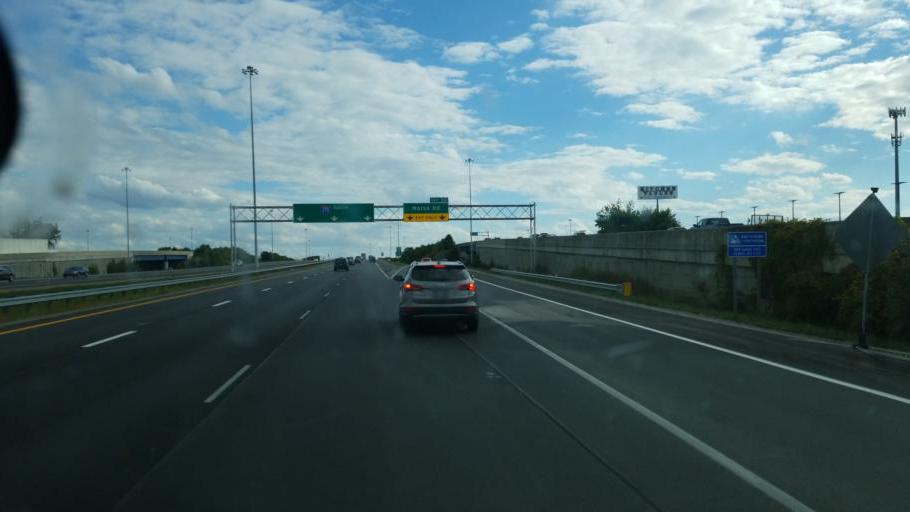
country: US
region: Ohio
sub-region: Franklin County
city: Huber Ridge
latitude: 40.0613
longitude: -82.9050
